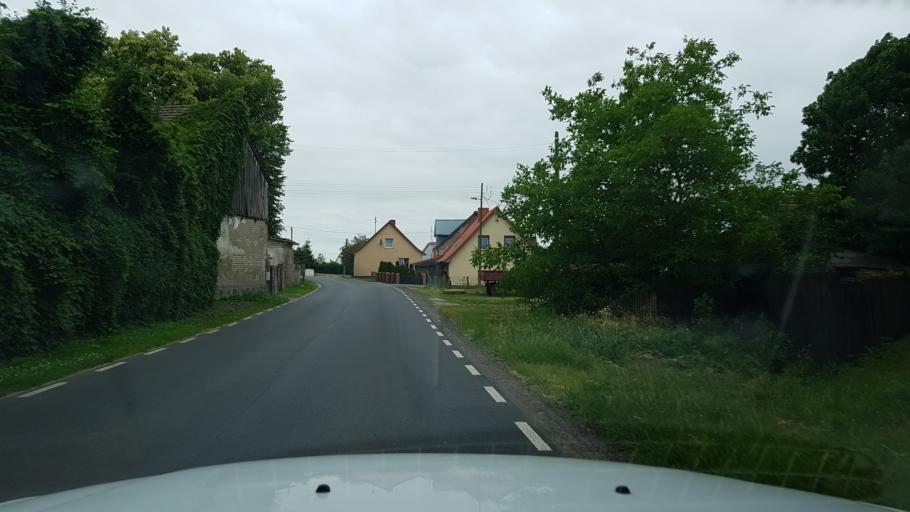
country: PL
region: West Pomeranian Voivodeship
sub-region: Powiat gryficki
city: Brojce
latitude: 53.9364
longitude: 15.4096
